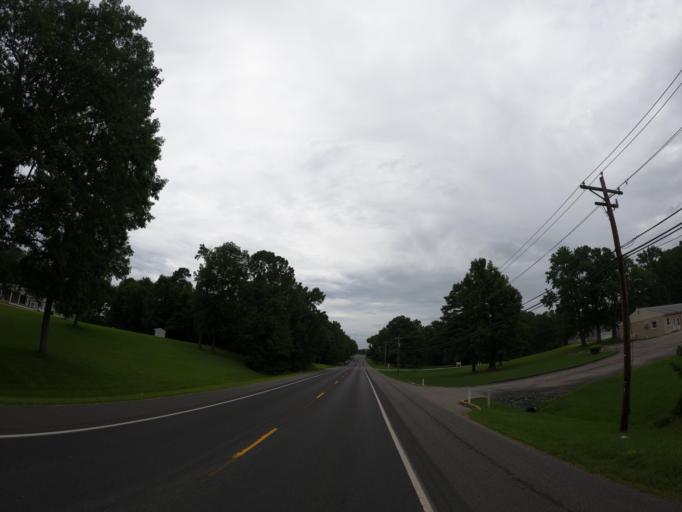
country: US
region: Maryland
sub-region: Saint Mary's County
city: Lexington Park
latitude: 38.2195
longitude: -76.5162
